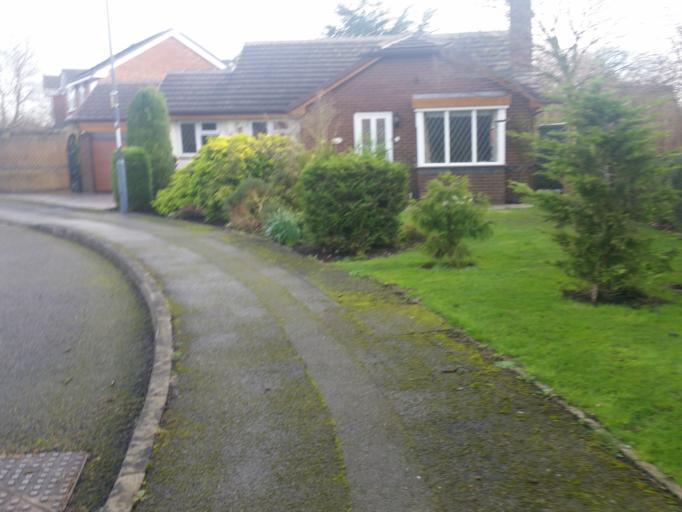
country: GB
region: England
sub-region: Derbyshire
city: Borrowash
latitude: 52.8893
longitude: -1.4092
